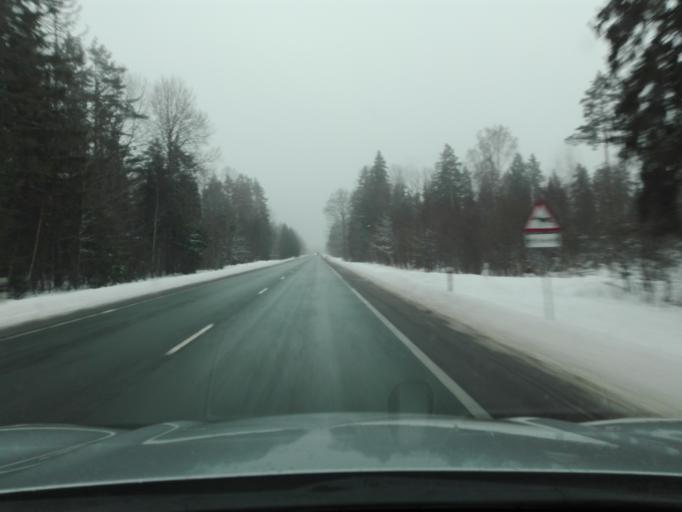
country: EE
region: Raplamaa
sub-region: Kohila vald
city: Kohila
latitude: 59.1520
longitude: 24.7806
